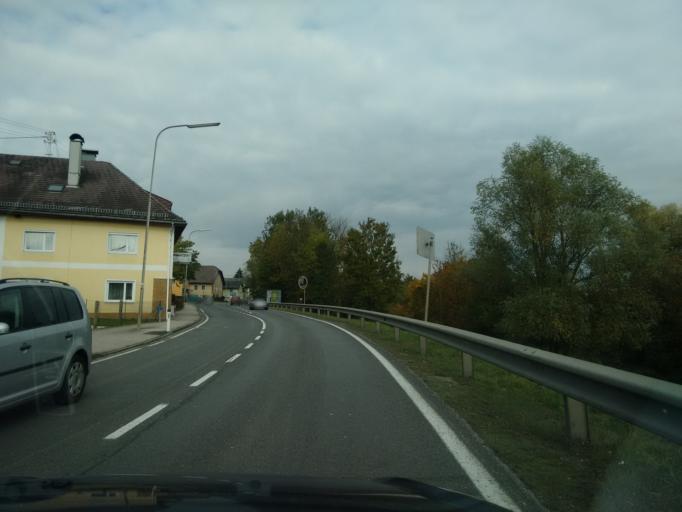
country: AT
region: Upper Austria
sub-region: Politischer Bezirk Vocklabruck
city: Timelkam
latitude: 47.9892
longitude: 13.6162
